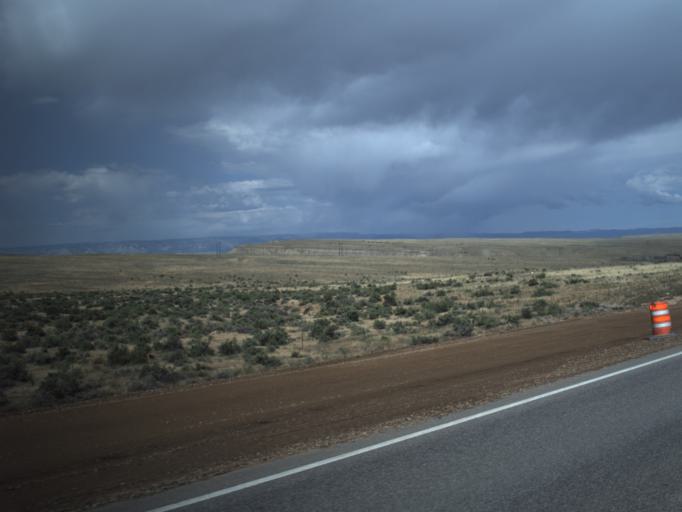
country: US
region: Utah
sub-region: Carbon County
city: East Carbon City
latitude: 39.4446
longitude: -110.4683
